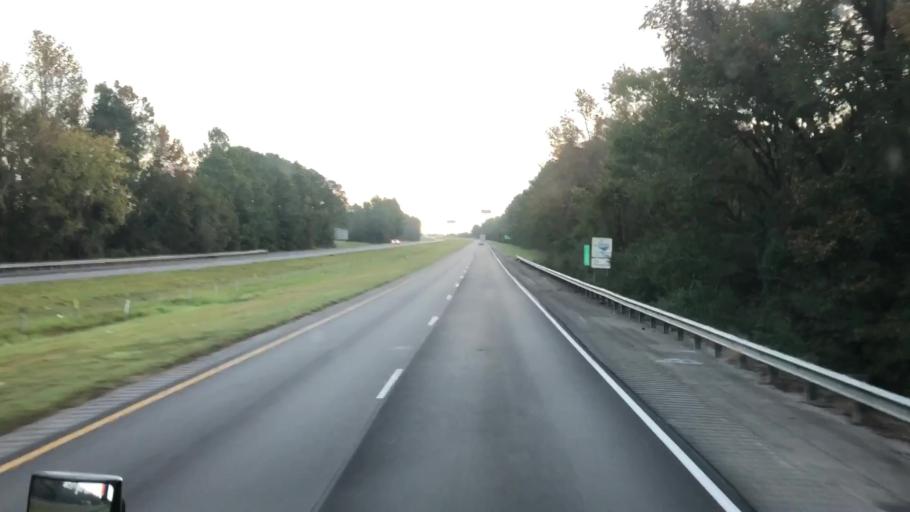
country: US
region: South Carolina
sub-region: Clarendon County
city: Manning
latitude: 33.5943
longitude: -80.3415
